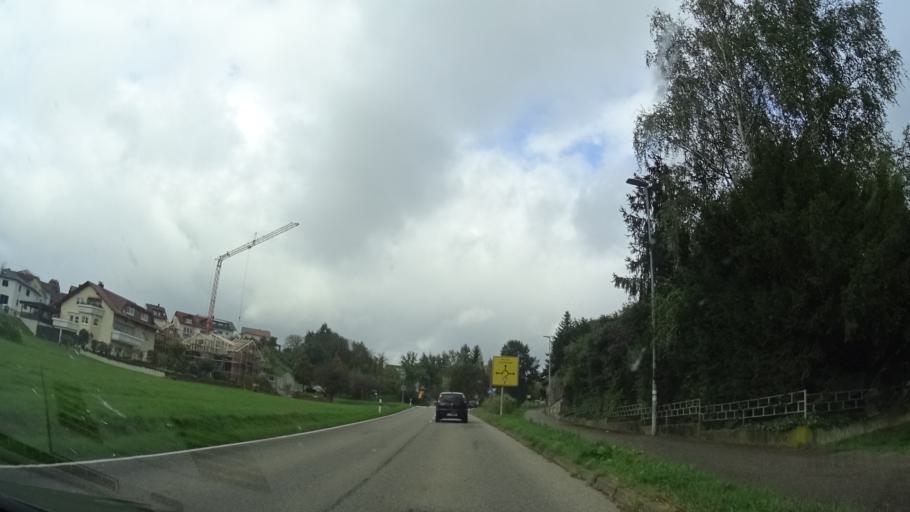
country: DE
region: Baden-Wuerttemberg
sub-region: Karlsruhe Region
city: Konigsbach-Stein
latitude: 48.9647
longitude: 8.6339
